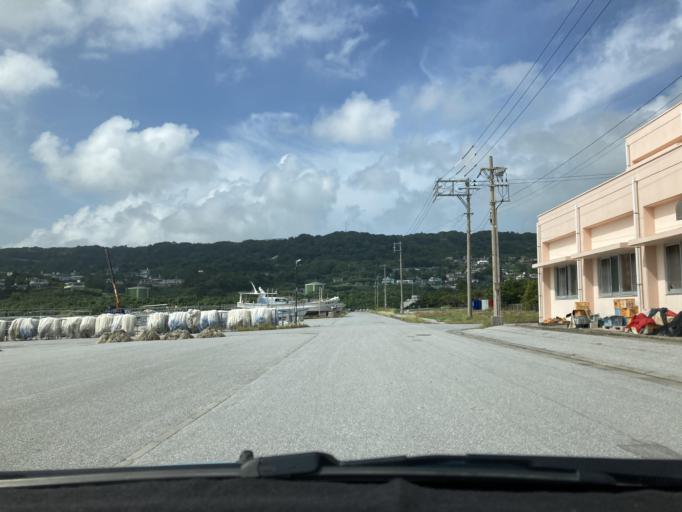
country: JP
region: Okinawa
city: Ginowan
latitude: 26.1485
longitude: 127.8083
